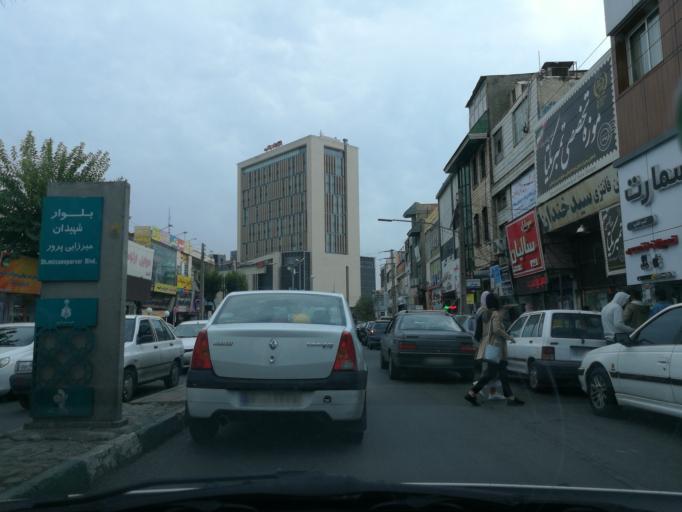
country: IR
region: Alborz
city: Karaj
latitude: 35.8451
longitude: 50.9706
